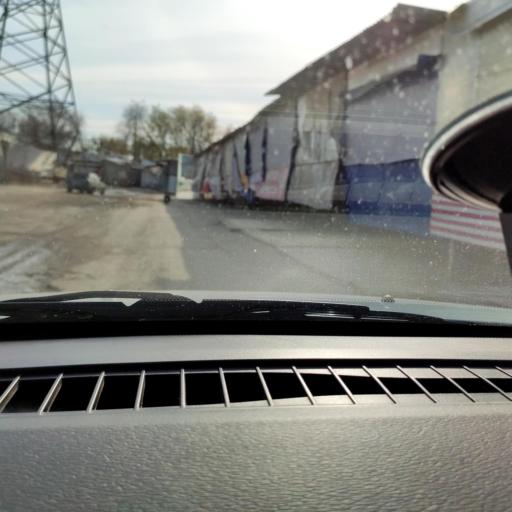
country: RU
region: Samara
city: Smyshlyayevka
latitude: 53.2118
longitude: 50.2742
